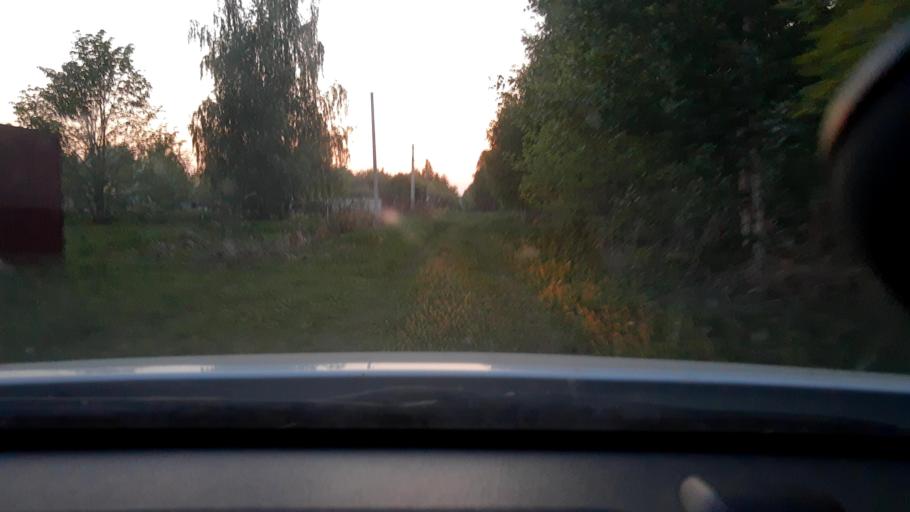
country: RU
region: Bashkortostan
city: Avdon
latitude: 54.5339
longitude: 55.8184
